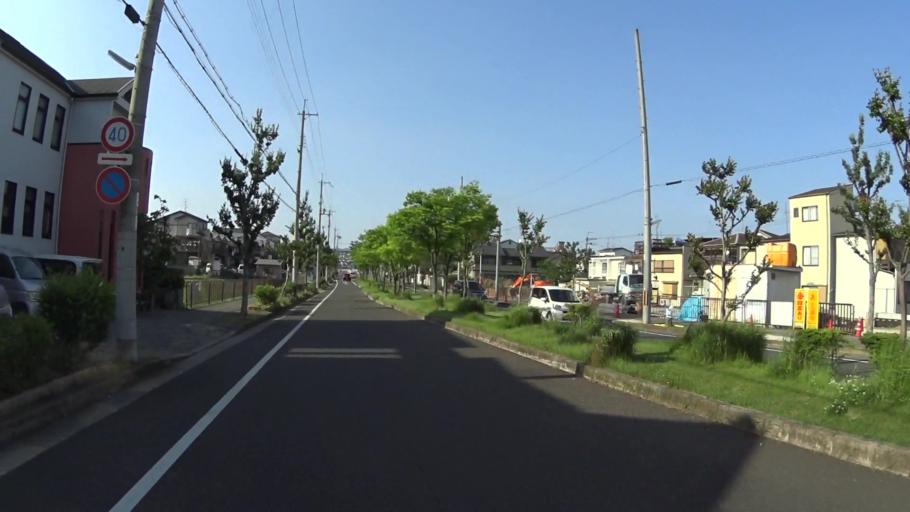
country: JP
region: Kyoto
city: Muko
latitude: 34.9403
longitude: 135.6914
